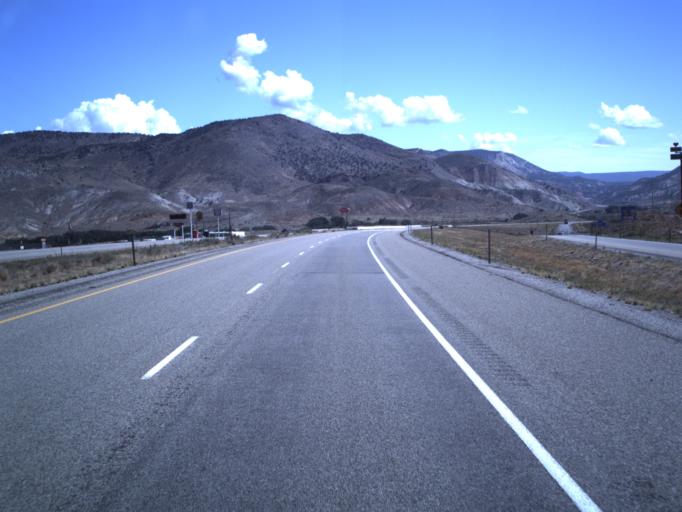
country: US
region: Utah
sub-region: Sevier County
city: Salina
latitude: 38.9332
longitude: -111.8588
